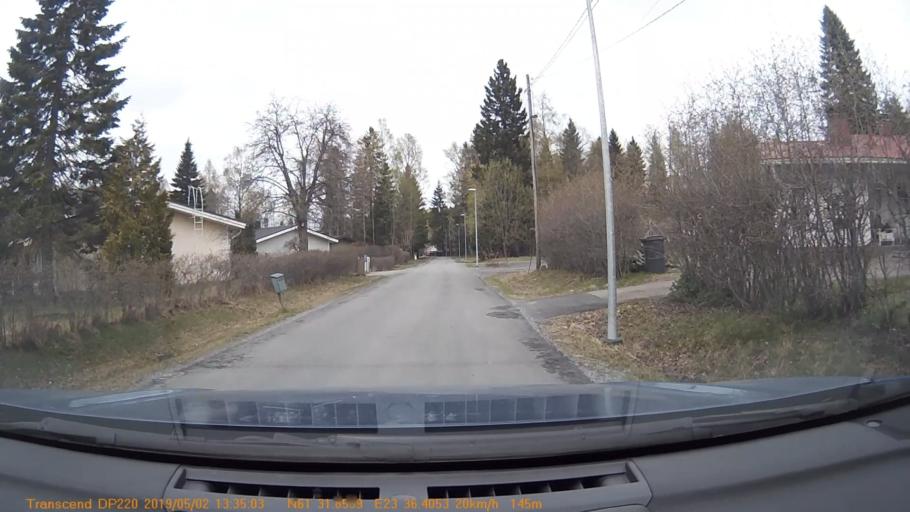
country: FI
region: Pirkanmaa
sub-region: Tampere
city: Yloejaervi
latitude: 61.5309
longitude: 23.6068
